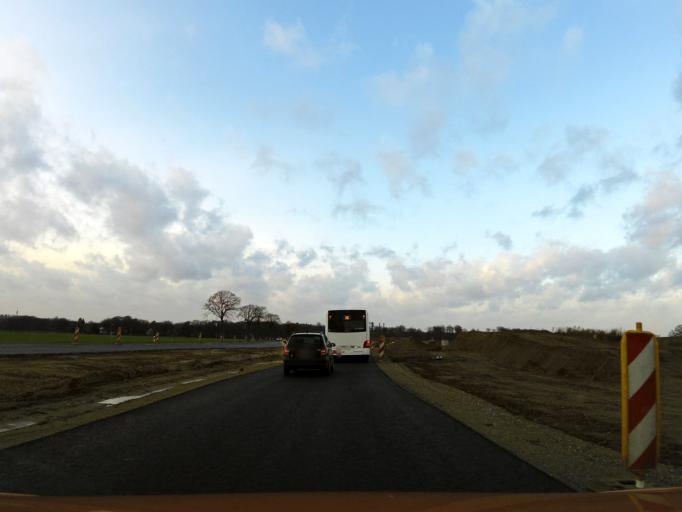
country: DE
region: Lower Saxony
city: Wolfsburg
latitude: 52.4115
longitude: 10.8220
